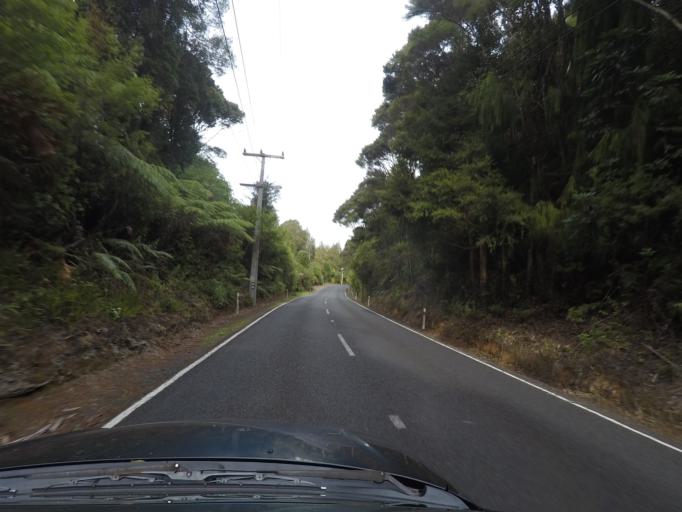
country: NZ
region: Auckland
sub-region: Auckland
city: Titirangi
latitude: -36.9401
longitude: 174.5824
